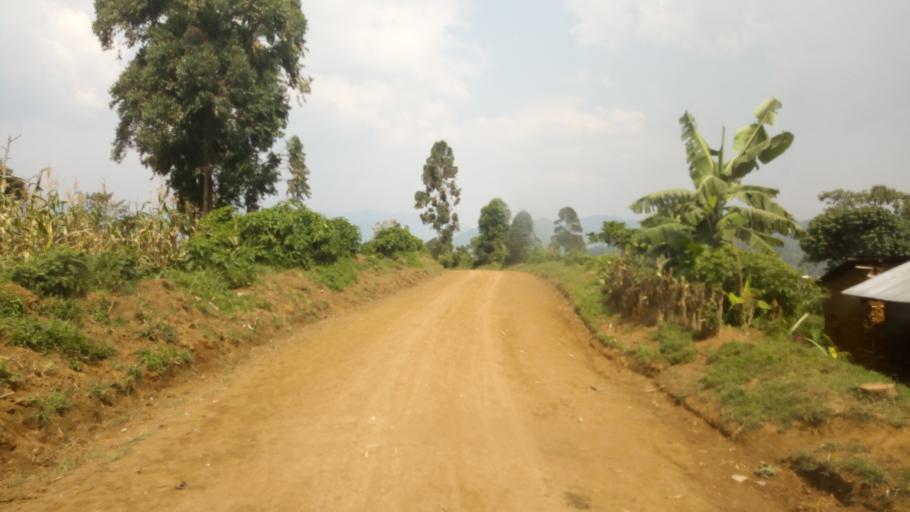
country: UG
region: Western Region
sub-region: Kanungu District
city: Ntungamo
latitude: -1.0203
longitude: 29.5850
